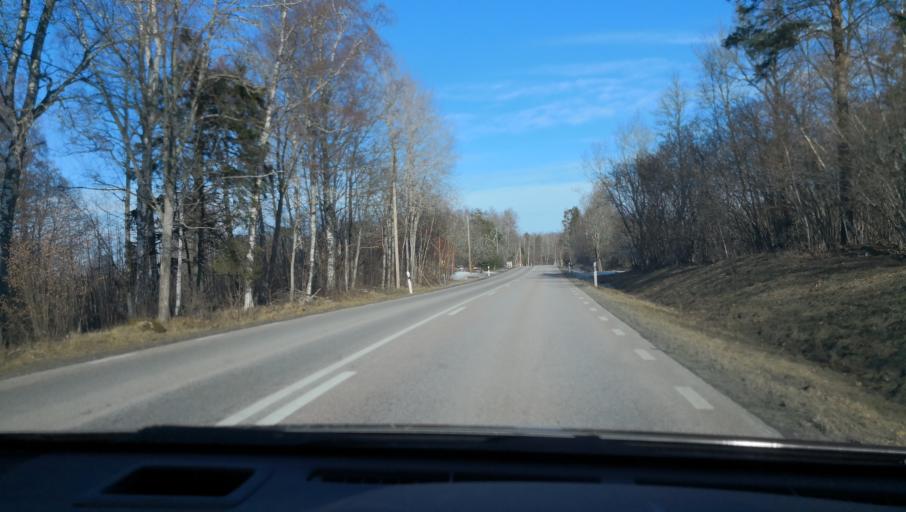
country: SE
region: Uppsala
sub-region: Osthammars Kommun
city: Osterbybruk
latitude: 60.1770
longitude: 17.8504
